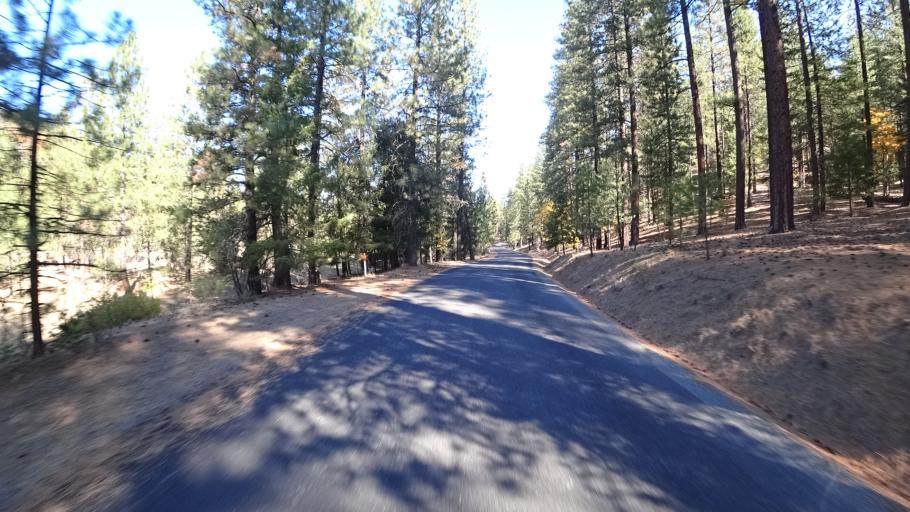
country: US
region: California
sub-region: Siskiyou County
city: Yreka
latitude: 41.6467
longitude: -122.8687
